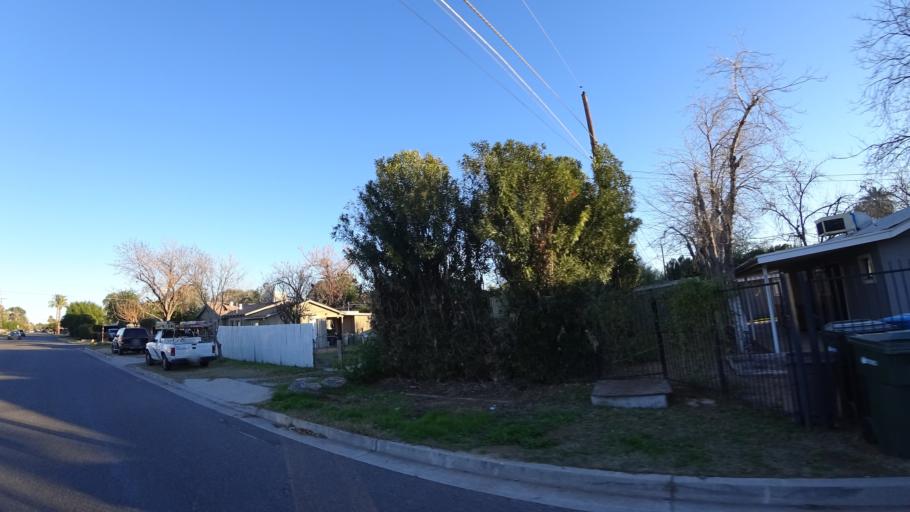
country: US
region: Arizona
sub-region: Maricopa County
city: Phoenix
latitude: 33.4767
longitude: -112.0201
